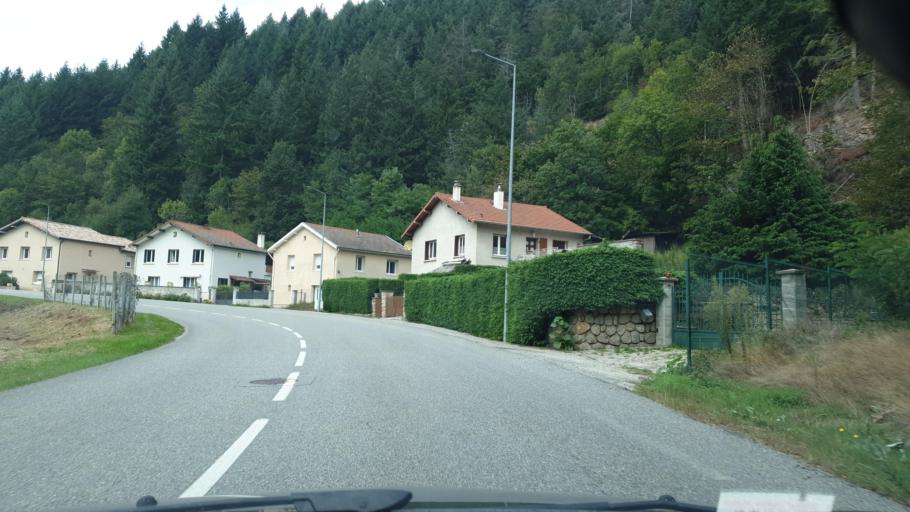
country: FR
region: Rhone-Alpes
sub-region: Departement de l'Ardeche
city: Le Cheylard
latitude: 44.8909
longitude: 4.3856
